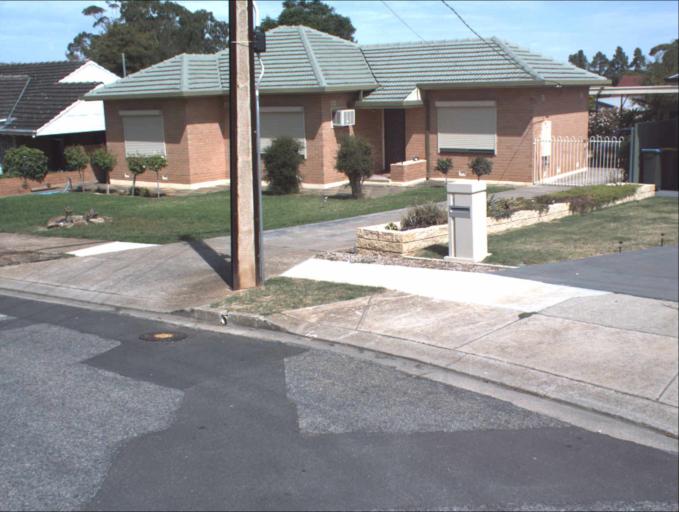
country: AU
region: South Australia
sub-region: Salisbury
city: Ingle Farm
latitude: -34.8429
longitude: 138.6238
